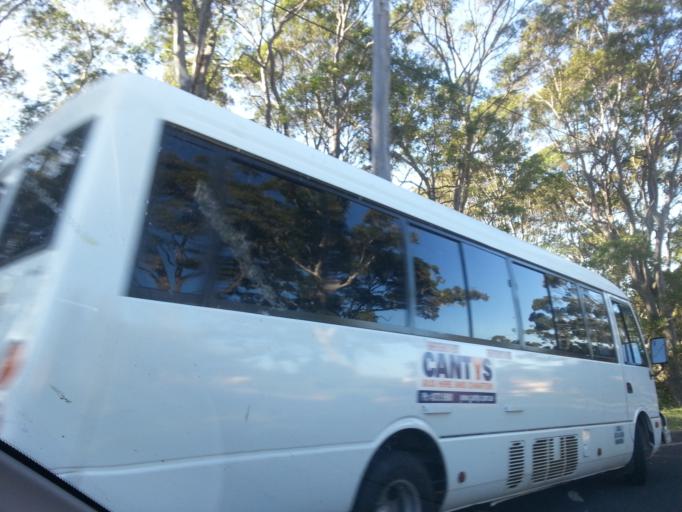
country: AU
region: New South Wales
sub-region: Wollongong
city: Mangerton
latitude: -34.4394
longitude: 150.8771
